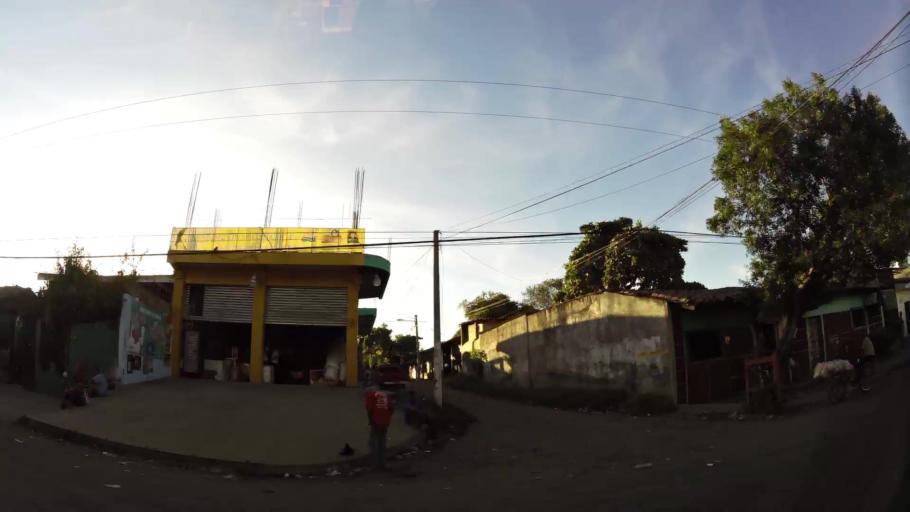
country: SV
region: San Miguel
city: San Miguel
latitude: 13.4667
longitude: -88.1755
